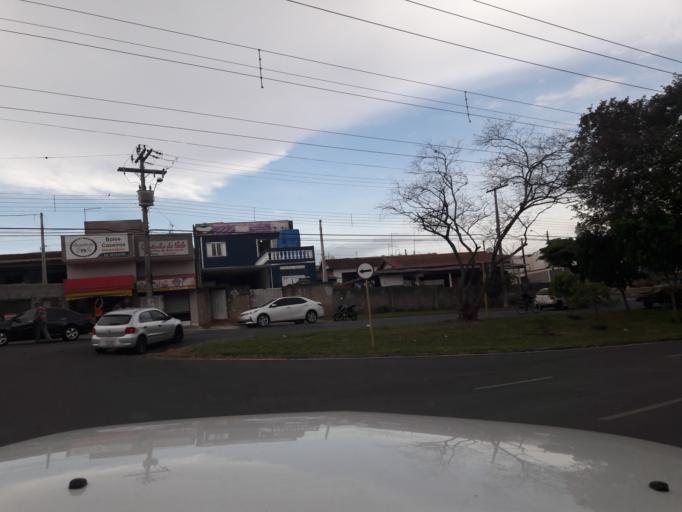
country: BR
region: Sao Paulo
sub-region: Moji-Guacu
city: Mogi-Gaucu
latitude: -22.3533
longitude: -46.9363
